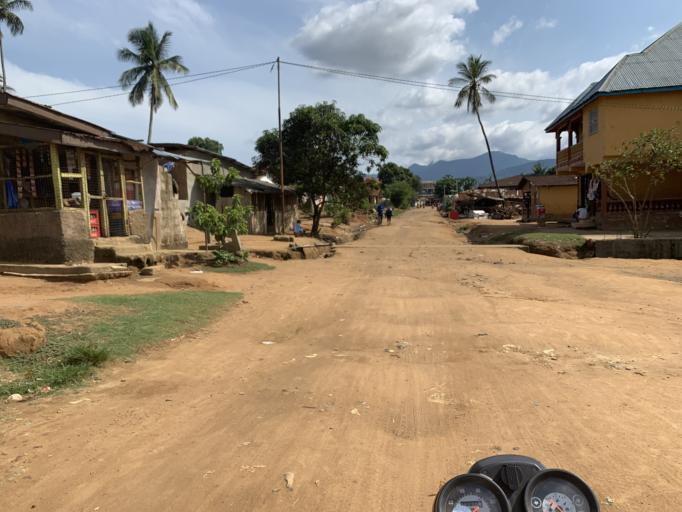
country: SL
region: Western Area
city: Waterloo
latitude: 8.3279
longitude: -13.0632
